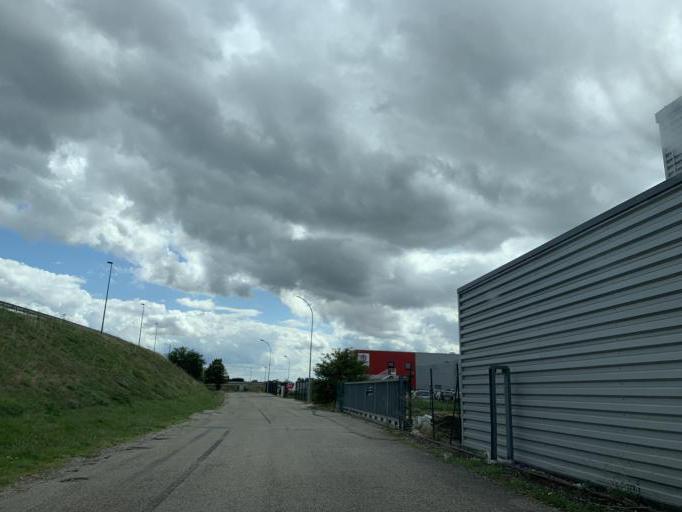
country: FR
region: Rhone-Alpes
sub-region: Departement de l'Ain
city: Montluel
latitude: 45.8447
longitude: 5.0655
